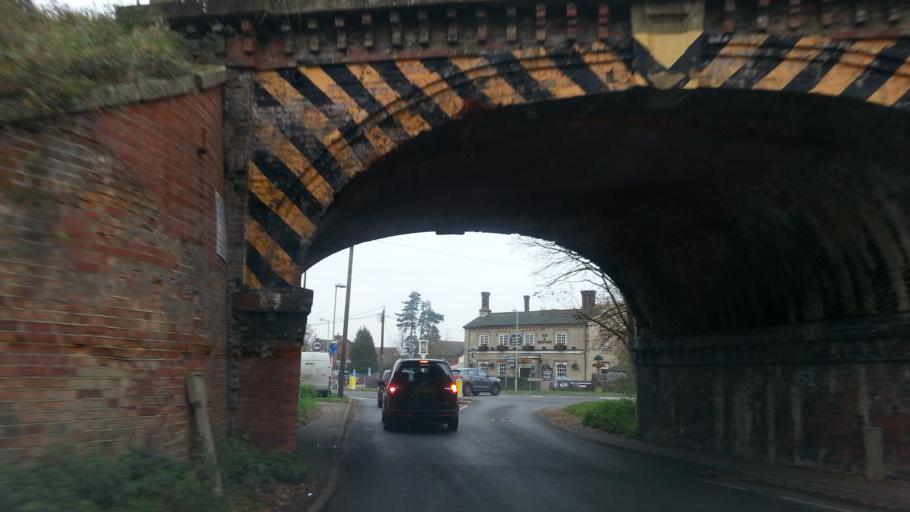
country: GB
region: England
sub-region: Suffolk
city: Thurston
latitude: 52.2498
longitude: 0.8078
